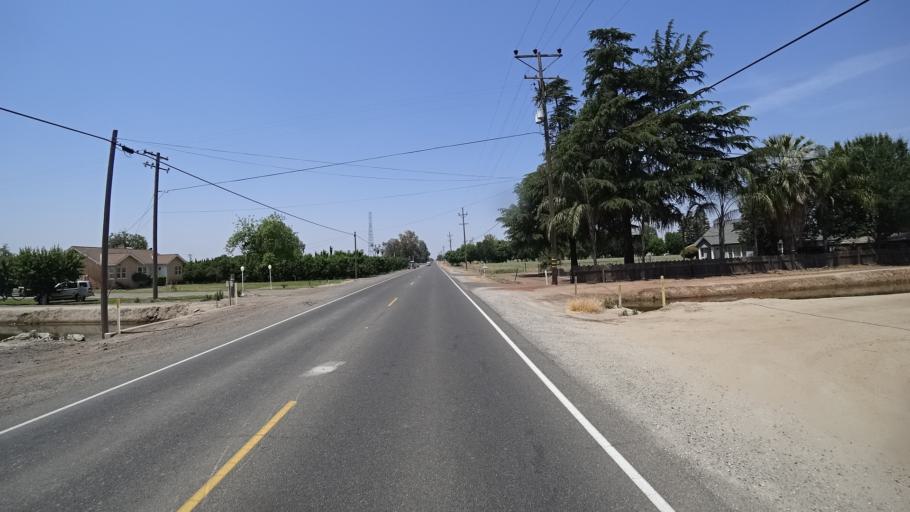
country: US
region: California
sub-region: Kings County
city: Armona
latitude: 36.3135
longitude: -119.7358
